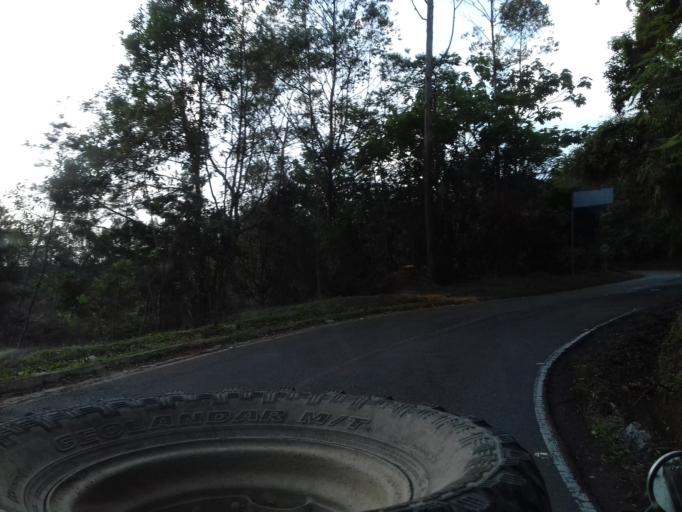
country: CO
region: Quindio
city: Salento
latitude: 4.6540
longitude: -75.5987
